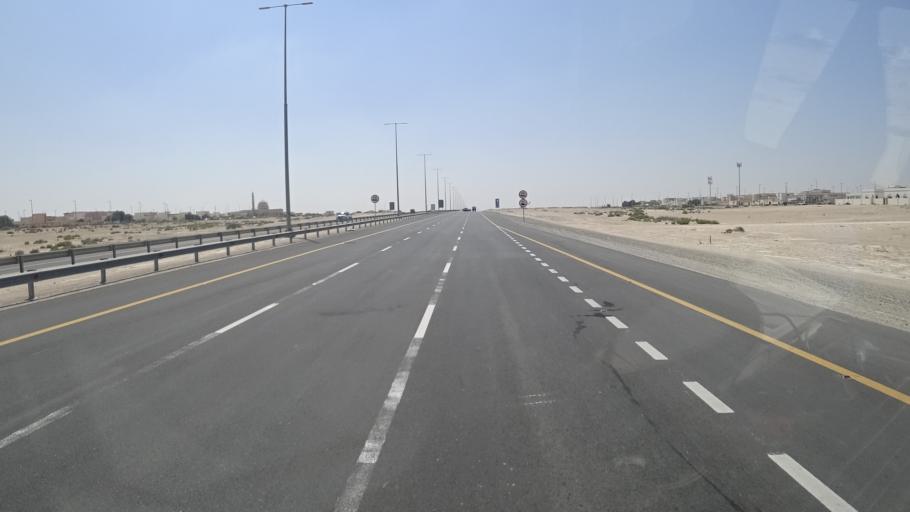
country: AE
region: Abu Dhabi
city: Abu Dhabi
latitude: 24.3318
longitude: 54.6942
